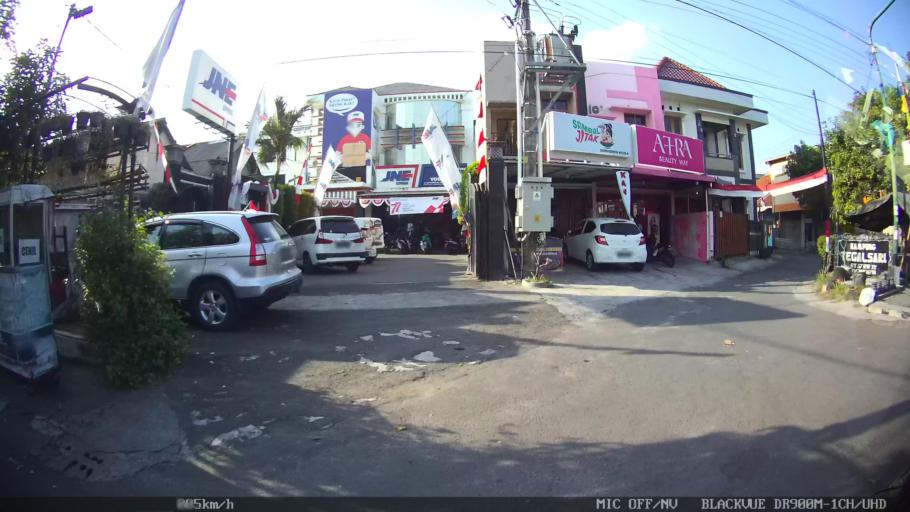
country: ID
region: Daerah Istimewa Yogyakarta
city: Yogyakarta
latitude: -7.8252
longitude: 110.3833
